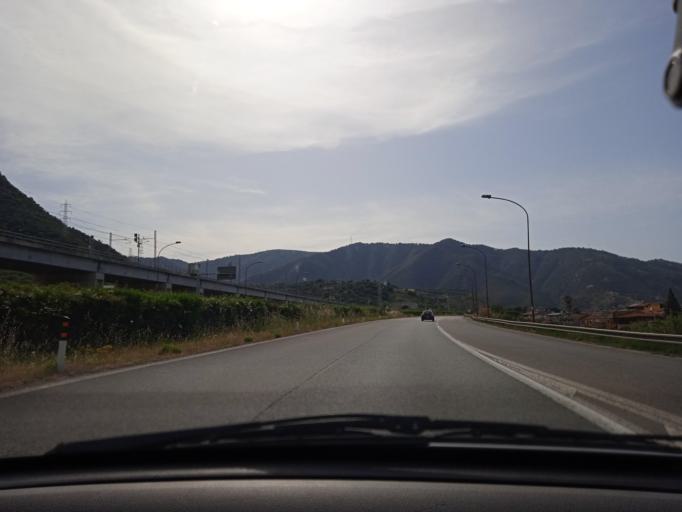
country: IT
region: Sicily
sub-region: Messina
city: Falcone
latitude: 38.1134
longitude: 15.0705
